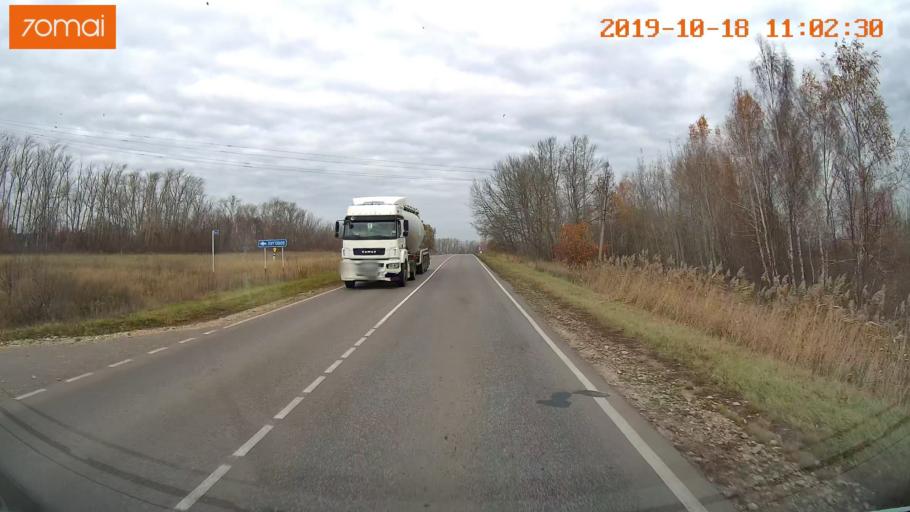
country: RU
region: Tula
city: Yepifan'
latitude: 53.8664
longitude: 38.5444
